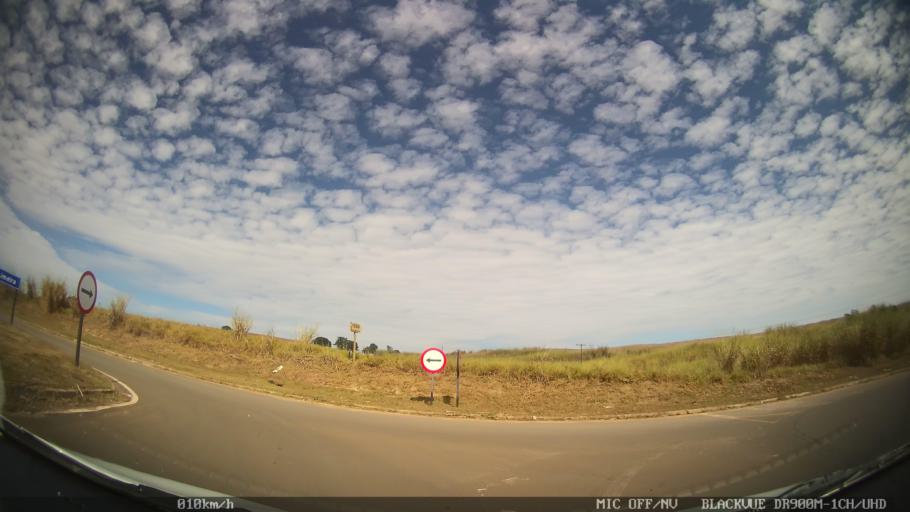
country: BR
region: Sao Paulo
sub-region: Santa Barbara D'Oeste
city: Santa Barbara d'Oeste
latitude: -22.6995
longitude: -47.4639
